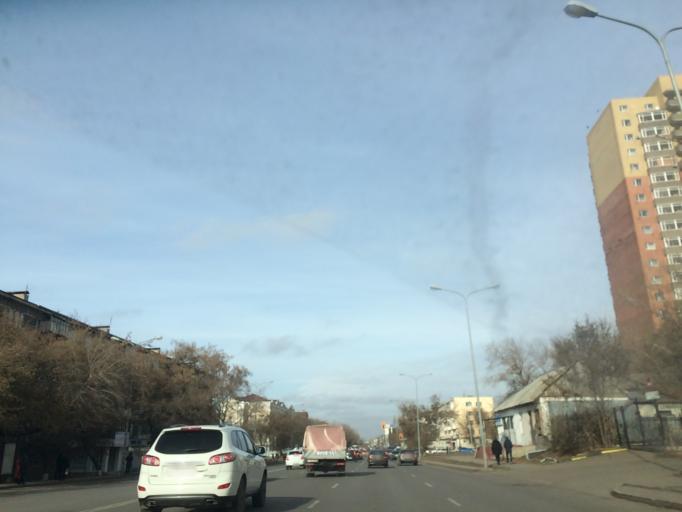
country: KZ
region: Astana Qalasy
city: Astana
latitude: 51.1757
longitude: 71.4245
